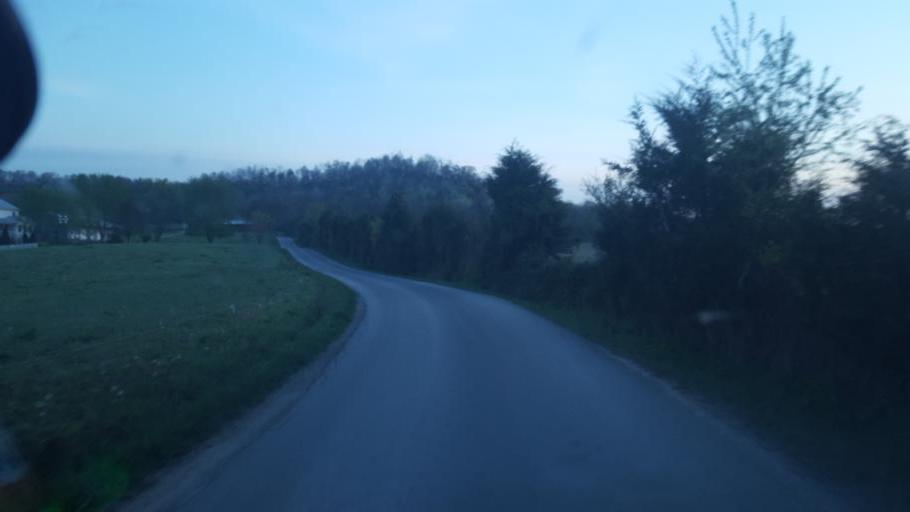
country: US
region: Kentucky
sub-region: Hart County
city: Munfordville
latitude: 37.2591
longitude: -85.9707
